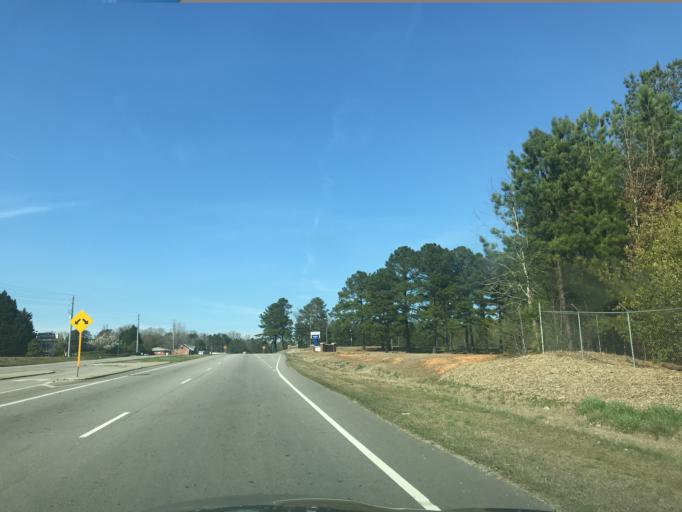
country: US
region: North Carolina
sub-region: Wake County
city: Fuquay-Varina
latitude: 35.6371
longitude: -78.7137
